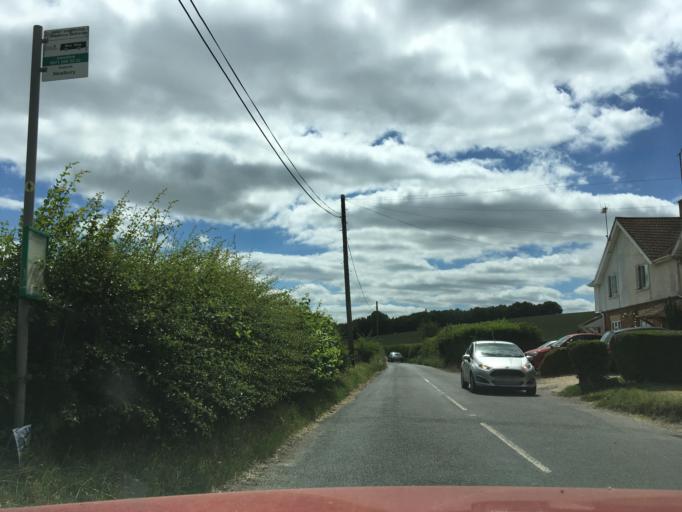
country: GB
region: England
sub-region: West Berkshire
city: Wickham
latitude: 51.4713
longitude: -1.4456
